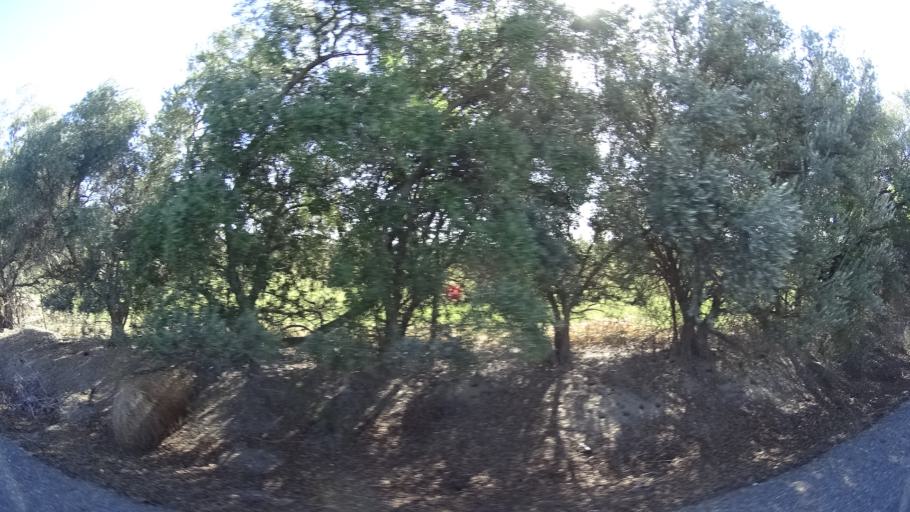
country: US
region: California
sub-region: Glenn County
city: Orland
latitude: 39.7635
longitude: -122.2478
